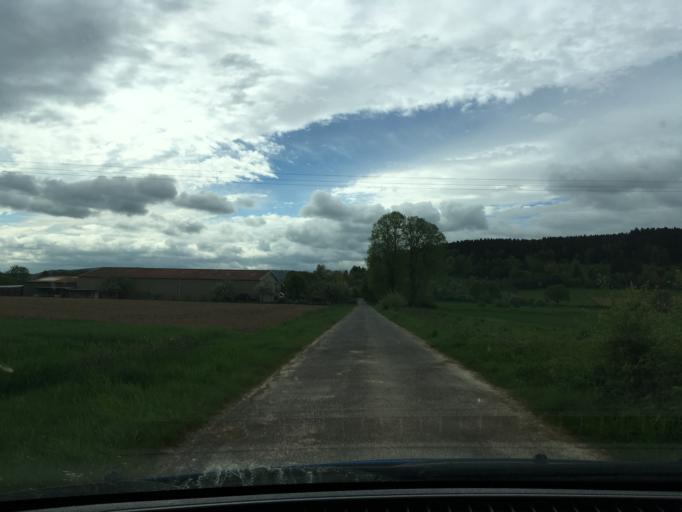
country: DE
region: Lower Saxony
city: Bodenfelde
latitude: 51.6554
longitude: 9.5412
